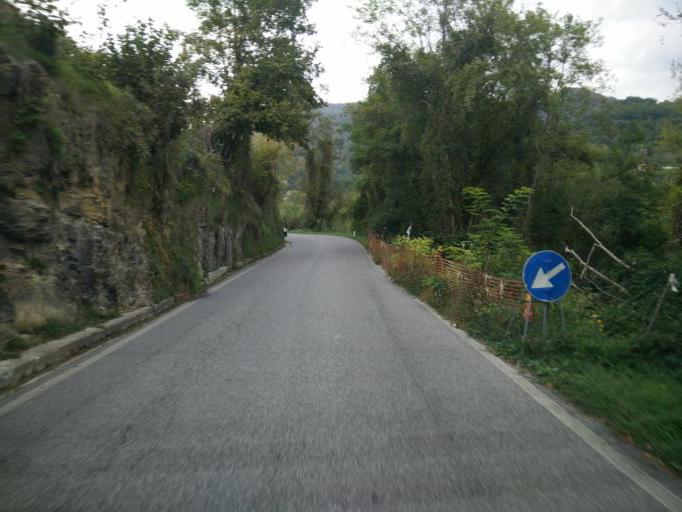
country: IT
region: Tuscany
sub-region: Provincia di Massa-Carrara
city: Casola in Lunigiana
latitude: 44.1900
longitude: 10.1423
